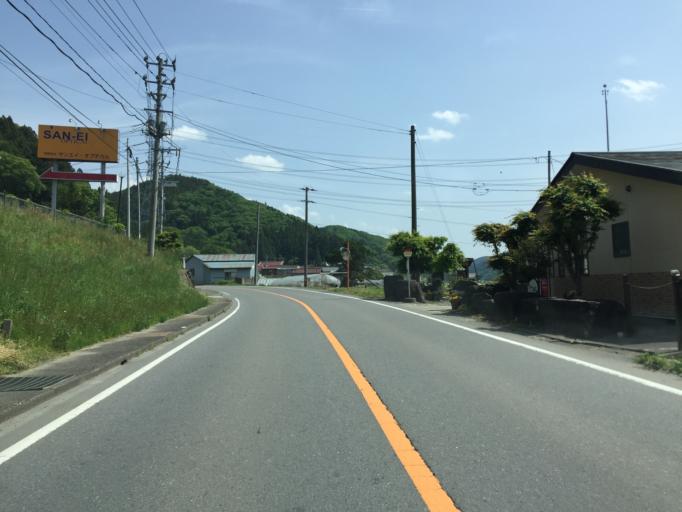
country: JP
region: Fukushima
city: Ishikawa
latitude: 37.1217
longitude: 140.5024
